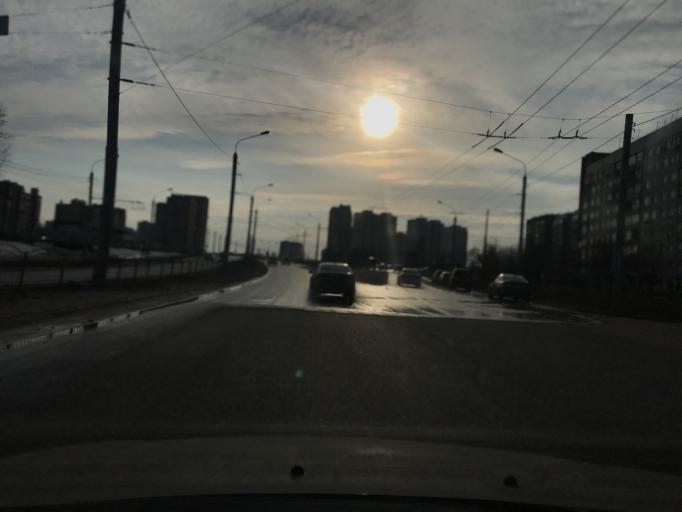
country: RU
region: Kaluga
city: Kaluga
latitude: 54.4915
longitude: 36.2120
